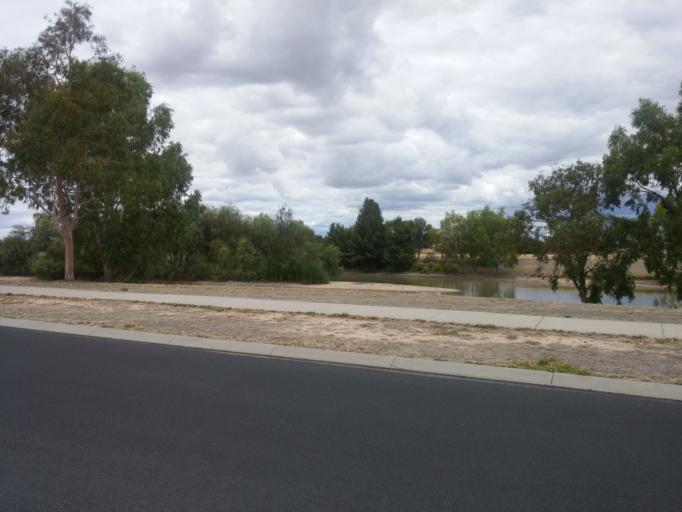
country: AU
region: Victoria
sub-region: Horsham
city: Horsham
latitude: -36.7290
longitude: 142.1978
